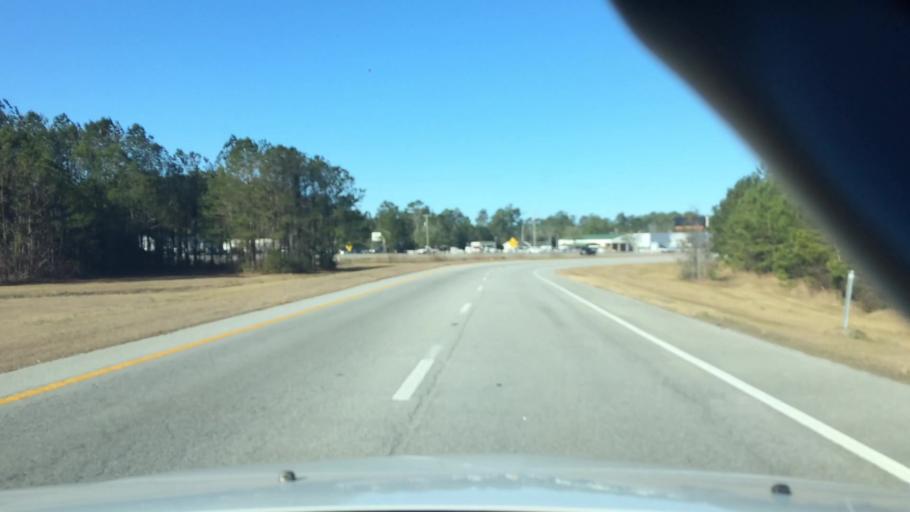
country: US
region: South Carolina
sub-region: Horry County
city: North Myrtle Beach
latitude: 33.8788
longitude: -78.6842
